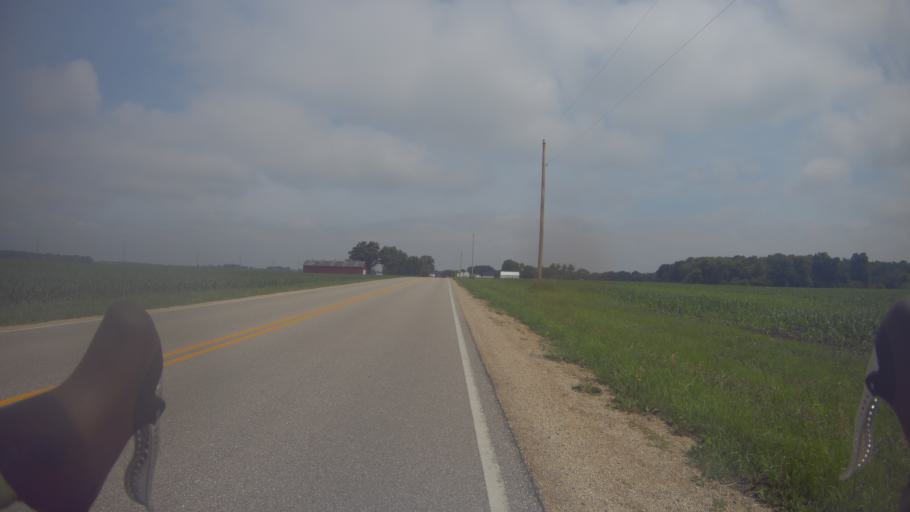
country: US
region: Wisconsin
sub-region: Rock County
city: Edgerton
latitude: 42.8798
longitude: -89.0389
